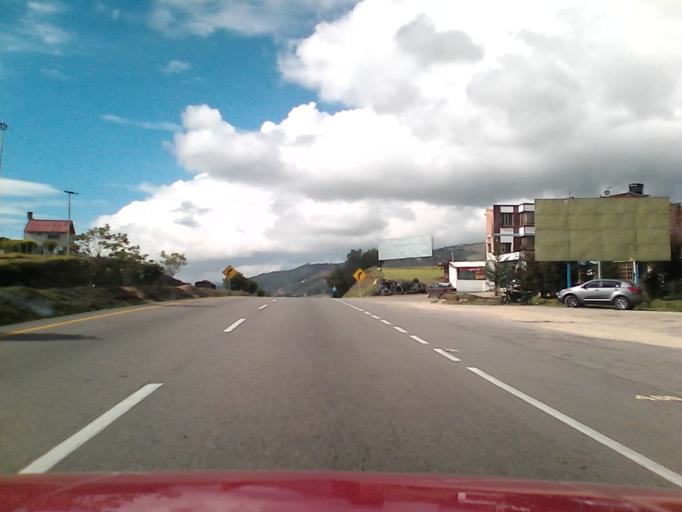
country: CO
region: Boyaca
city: Combita
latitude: 5.6205
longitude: -73.3118
